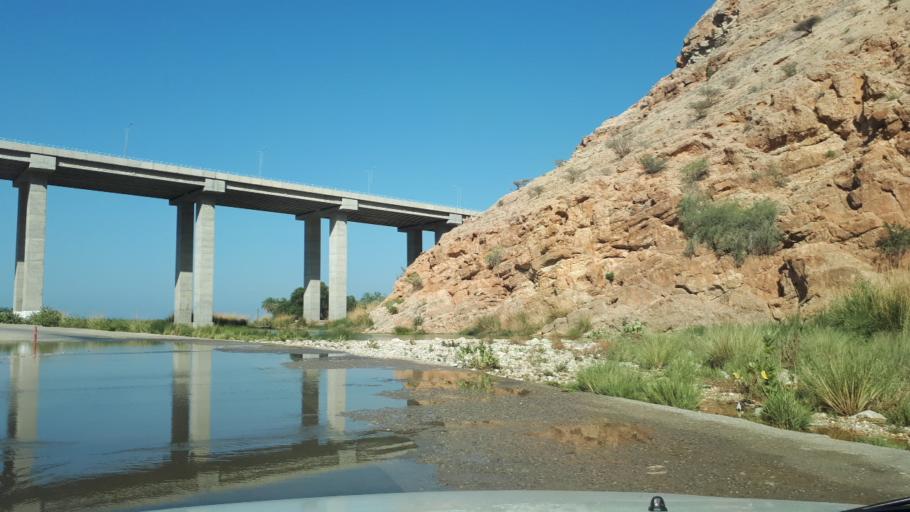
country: OM
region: Ash Sharqiyah
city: Sur
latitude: 22.8235
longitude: 59.2597
